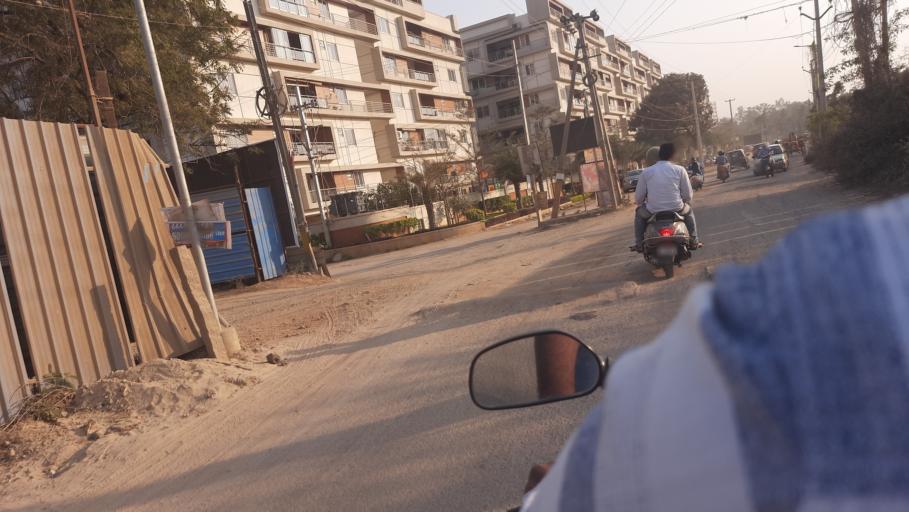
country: IN
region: Telangana
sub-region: Rangareddi
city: Secunderabad
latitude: 17.5209
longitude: 78.5413
